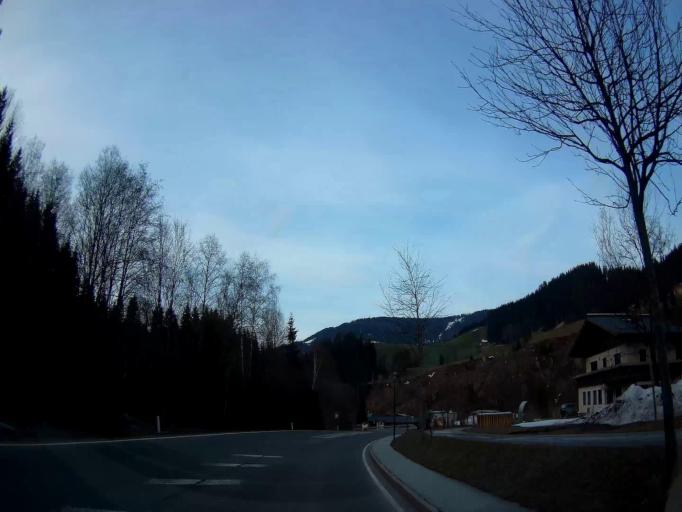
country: AT
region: Salzburg
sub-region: Politischer Bezirk Hallein
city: Abtenau
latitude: 47.5304
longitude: 13.4249
